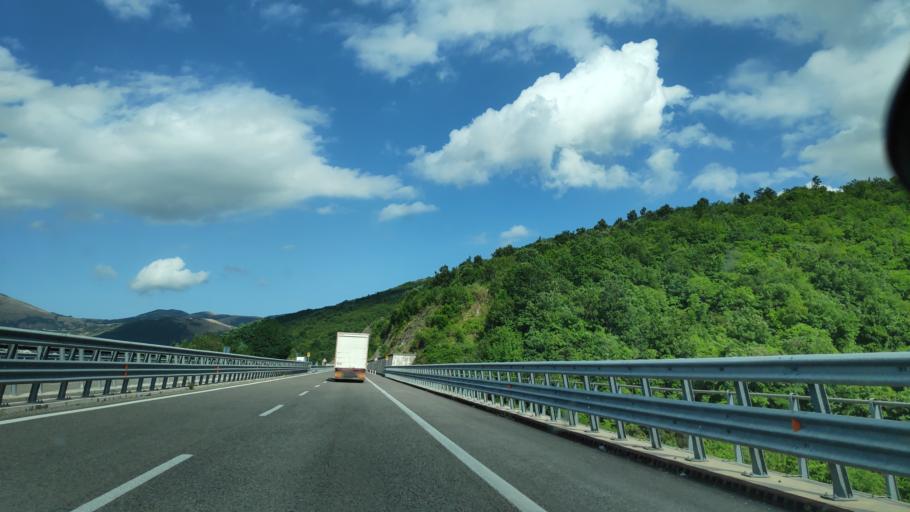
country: IT
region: Campania
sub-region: Provincia di Salerno
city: Pertosa
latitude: 40.5313
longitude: 15.4457
